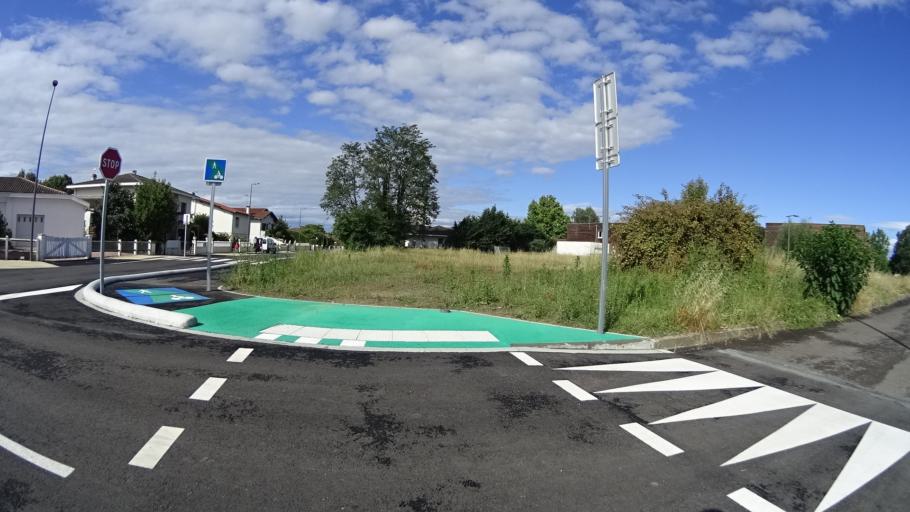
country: FR
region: Aquitaine
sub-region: Departement des Landes
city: Dax
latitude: 43.7004
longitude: -1.0686
